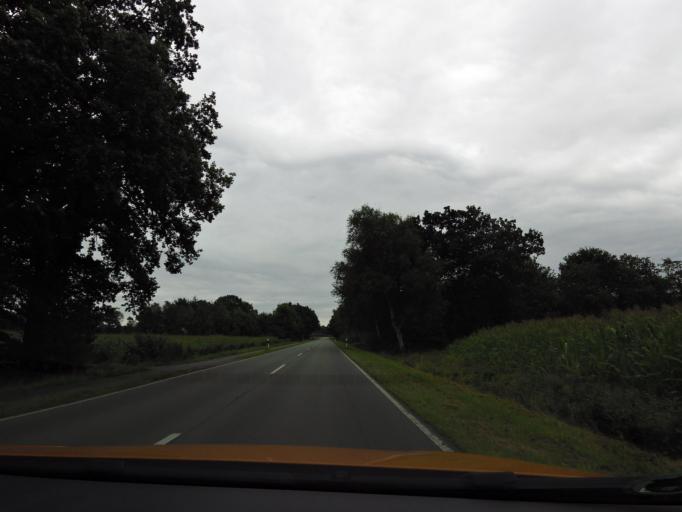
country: DE
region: Lower Saxony
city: Westerstede
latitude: 53.2421
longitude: 7.9827
